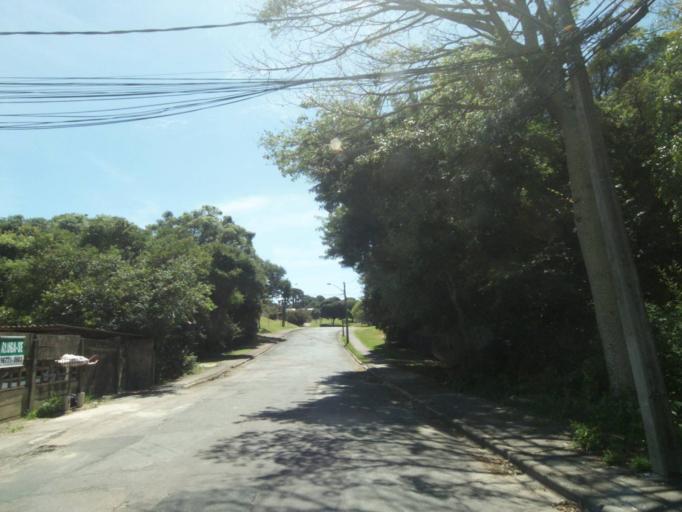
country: BR
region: Parana
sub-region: Curitiba
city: Curitiba
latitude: -25.4665
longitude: -49.2408
